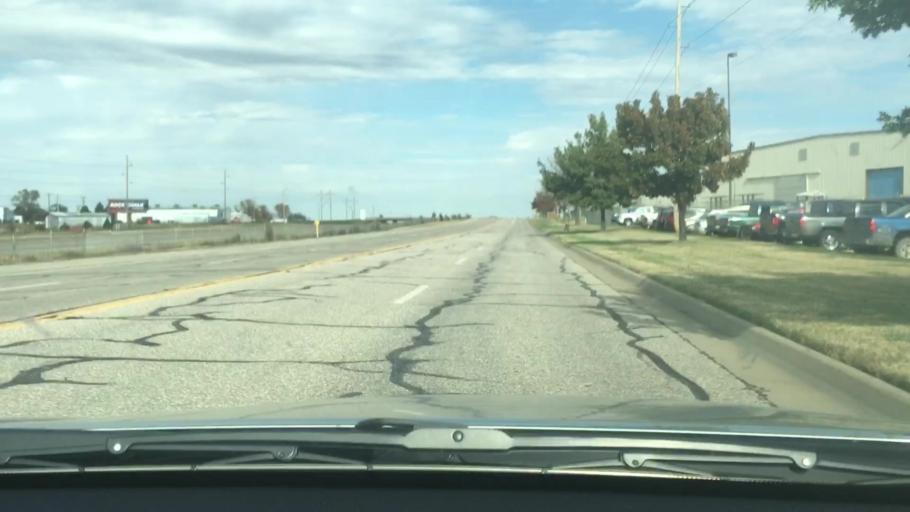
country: US
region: Kansas
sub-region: Sedgwick County
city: Wichita
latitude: 37.6301
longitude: -97.2884
